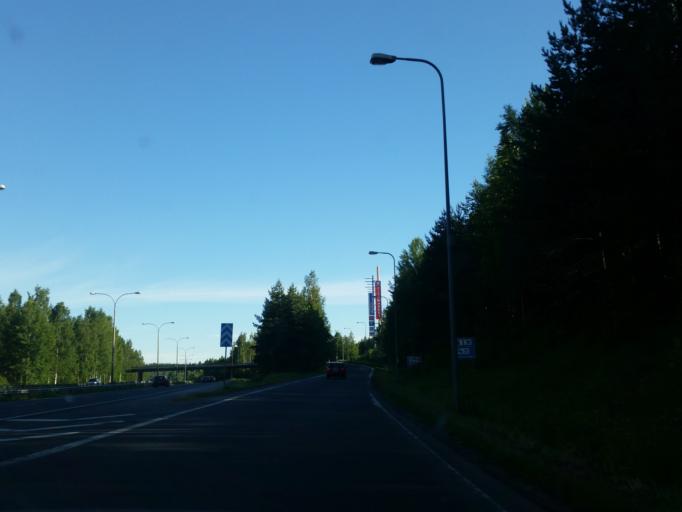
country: FI
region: Northern Savo
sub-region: Kuopio
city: Kuopio
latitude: 62.8646
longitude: 27.6179
